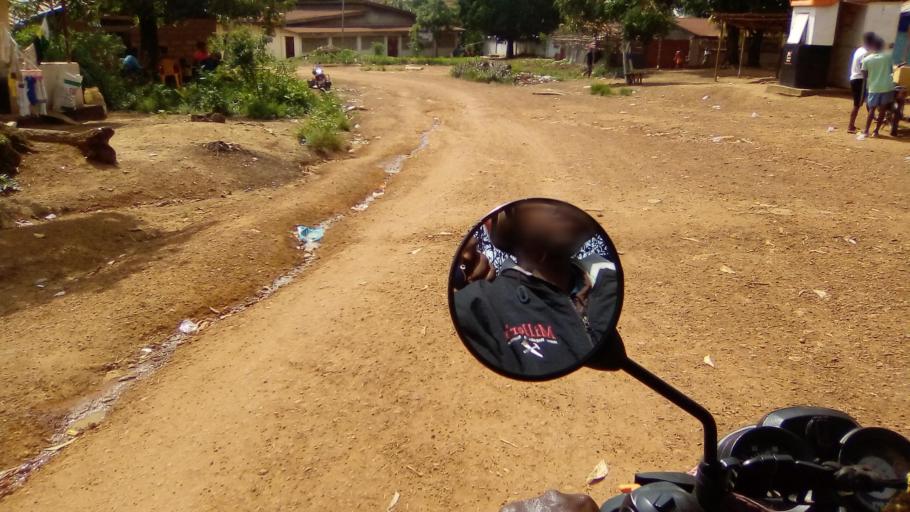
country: SL
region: Southern Province
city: Bo
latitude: 7.9489
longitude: -11.7203
